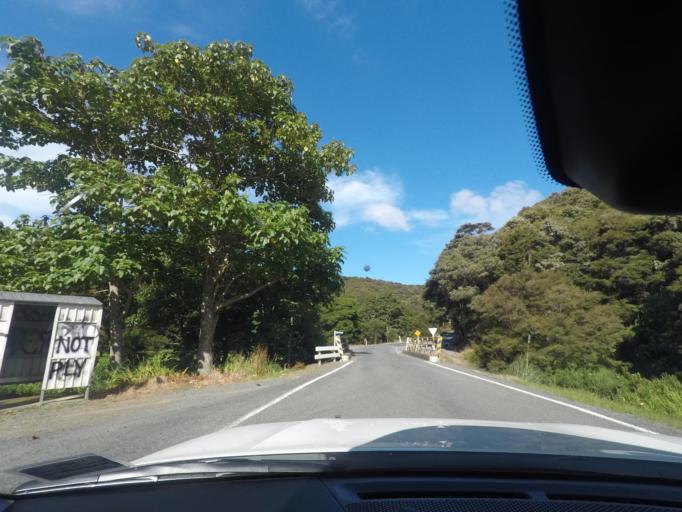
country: NZ
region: Northland
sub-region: Whangarei
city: Ngunguru
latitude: -35.6687
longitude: 174.4542
